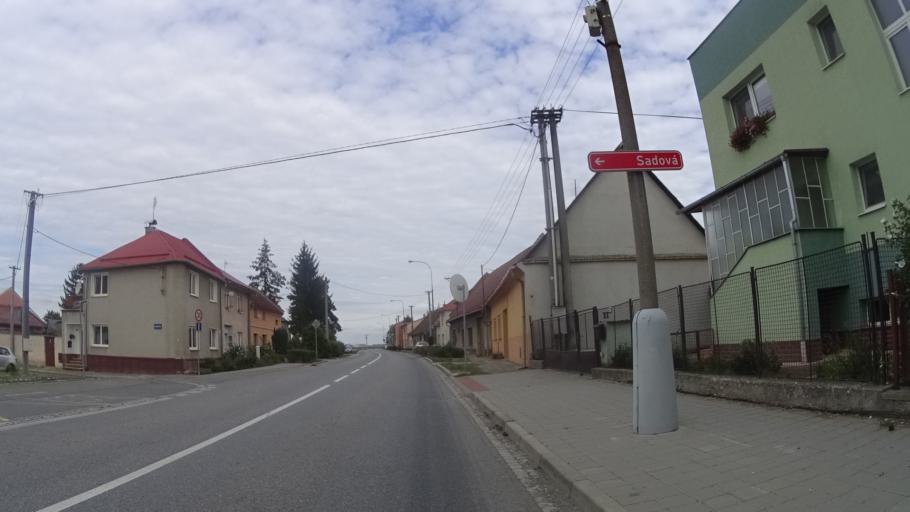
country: CZ
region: Olomoucky
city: Tovacov
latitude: 49.4372
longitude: 17.2843
